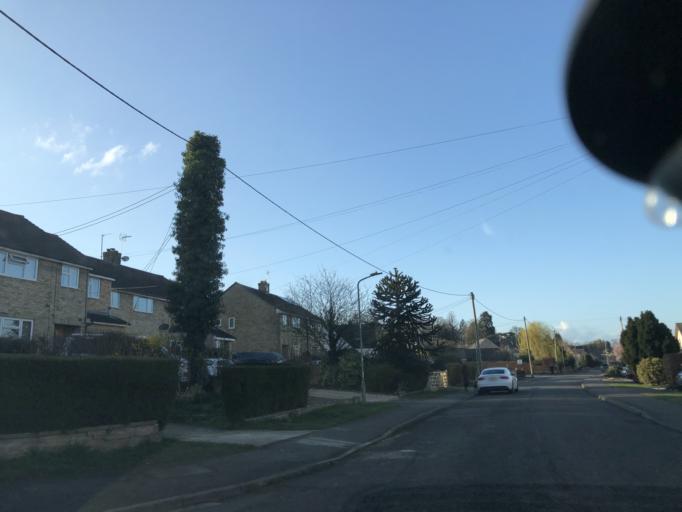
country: GB
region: England
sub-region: Oxfordshire
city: Witney
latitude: 51.7820
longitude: -1.4971
